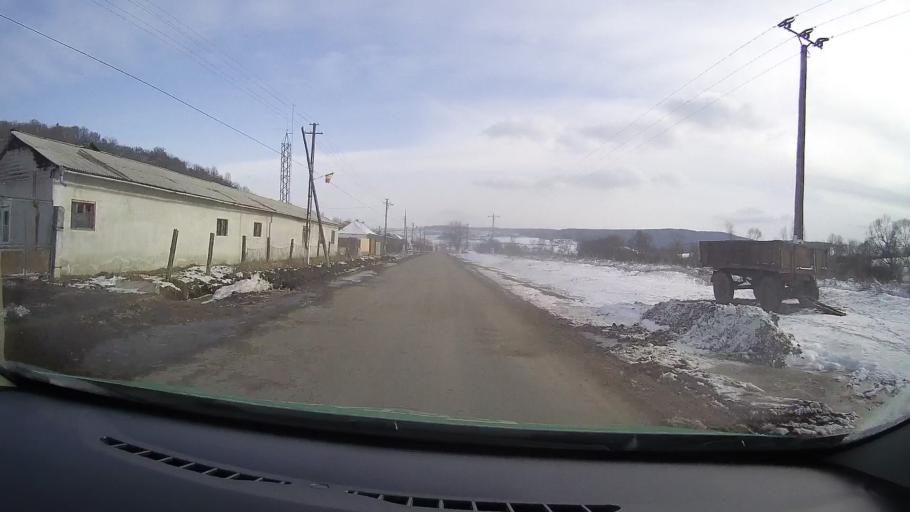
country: RO
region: Sibiu
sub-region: Comuna Iacobeni
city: Iacobeni
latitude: 46.0461
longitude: 24.7247
